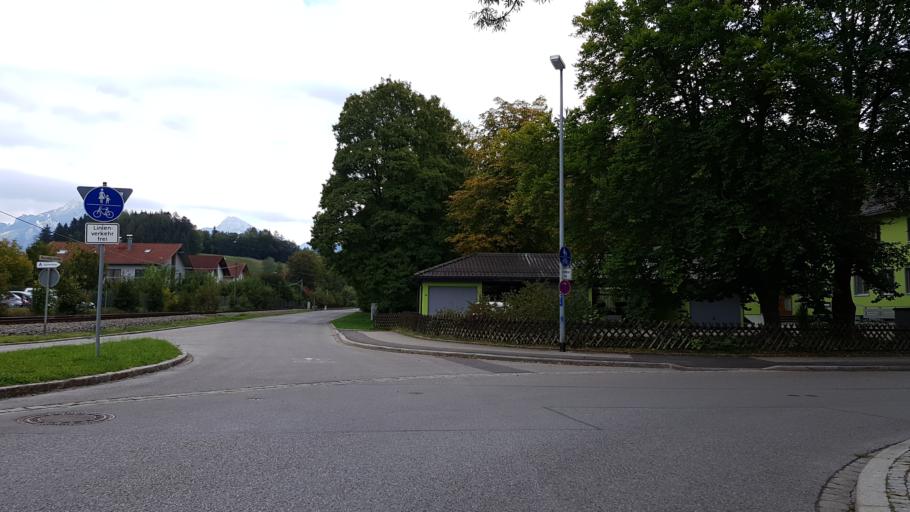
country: DE
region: Bavaria
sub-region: Swabia
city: Fuessen
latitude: 47.5744
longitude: 10.6872
